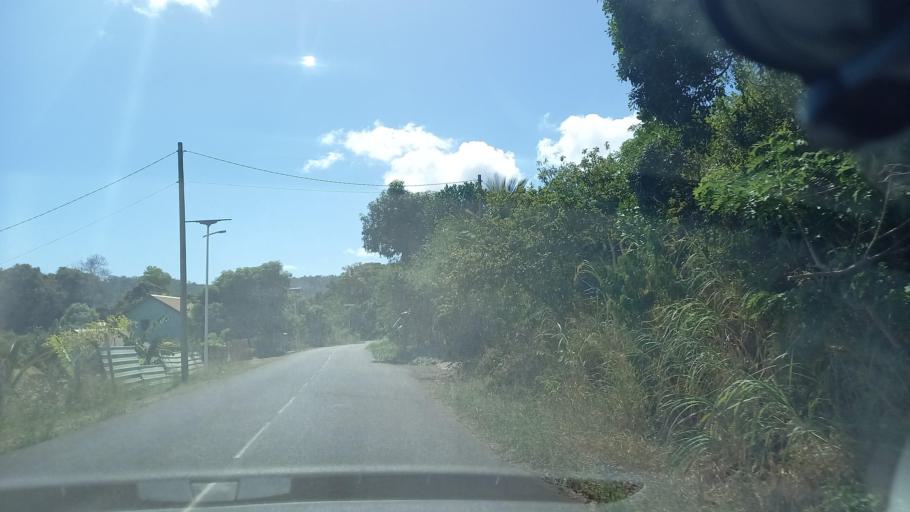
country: YT
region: Kani-Keli
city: Kani Keli
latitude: -12.9648
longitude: 45.1136
